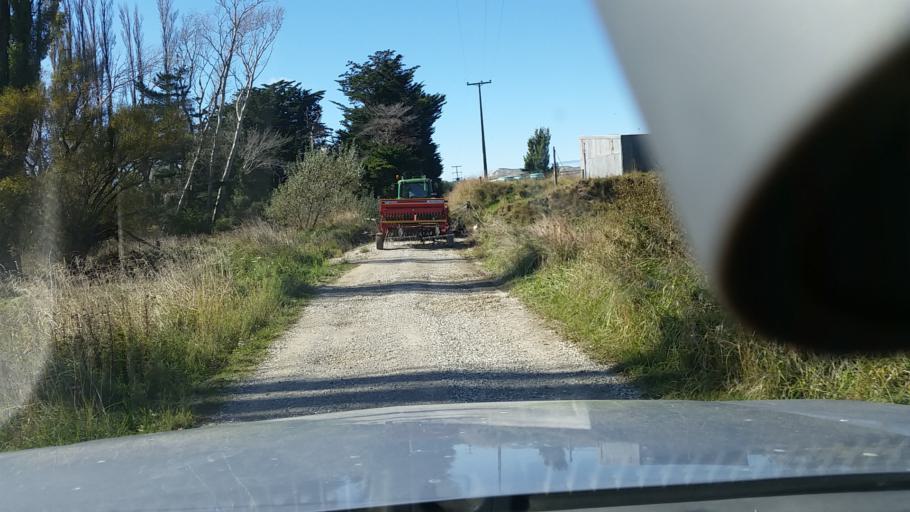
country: NZ
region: Marlborough
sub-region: Marlborough District
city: Blenheim
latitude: -41.8248
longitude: 174.1286
